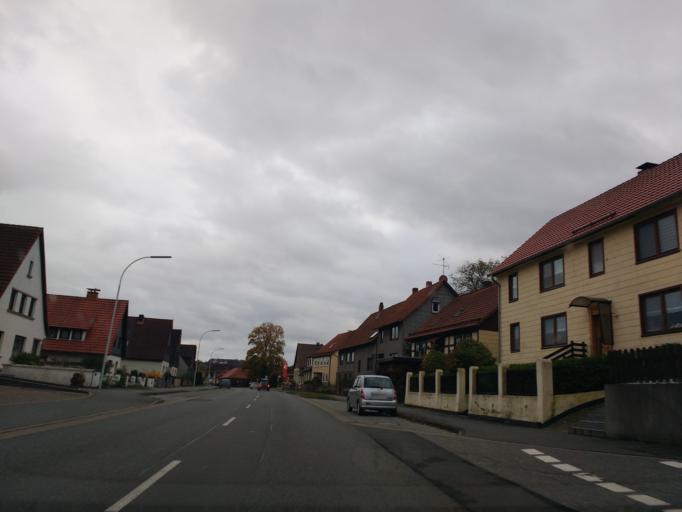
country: DE
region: Lower Saxony
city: Bad Lauterberg im Harz
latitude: 51.6175
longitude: 10.4157
